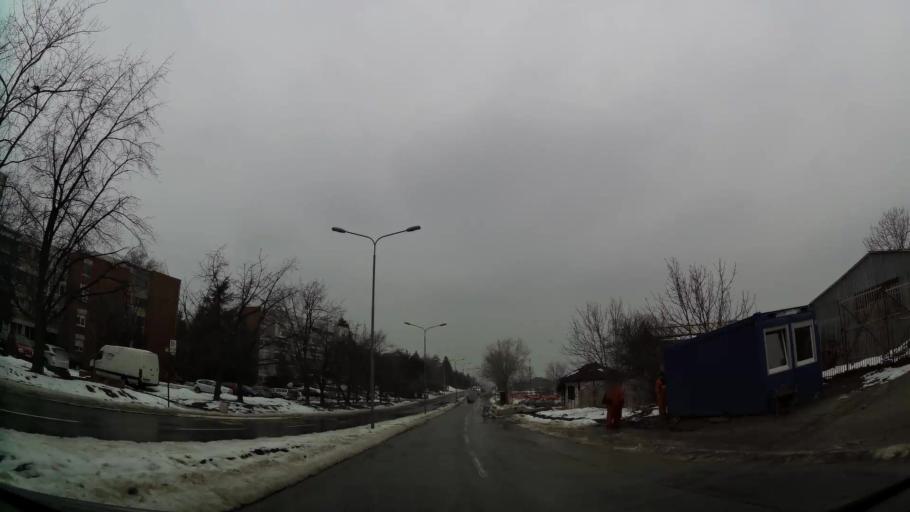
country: RS
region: Central Serbia
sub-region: Belgrade
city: Zvezdara
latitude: 44.7518
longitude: 20.5030
